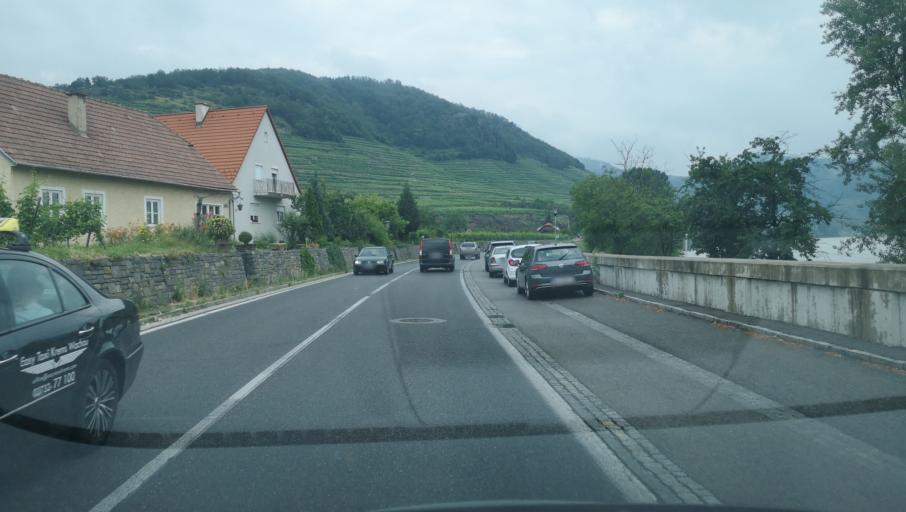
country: AT
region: Lower Austria
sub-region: Politischer Bezirk Krems
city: Weinzierl am Walde
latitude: 48.3976
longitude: 15.4740
